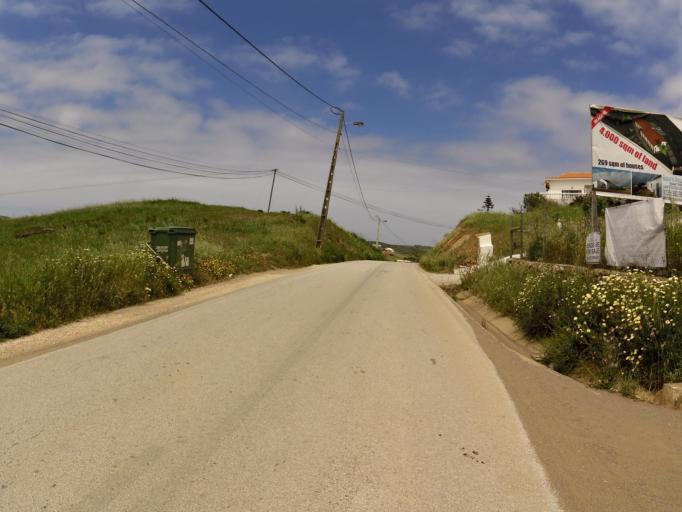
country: PT
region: Faro
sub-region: Vila do Bispo
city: Vila do Bispo
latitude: 37.0800
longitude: -8.8886
